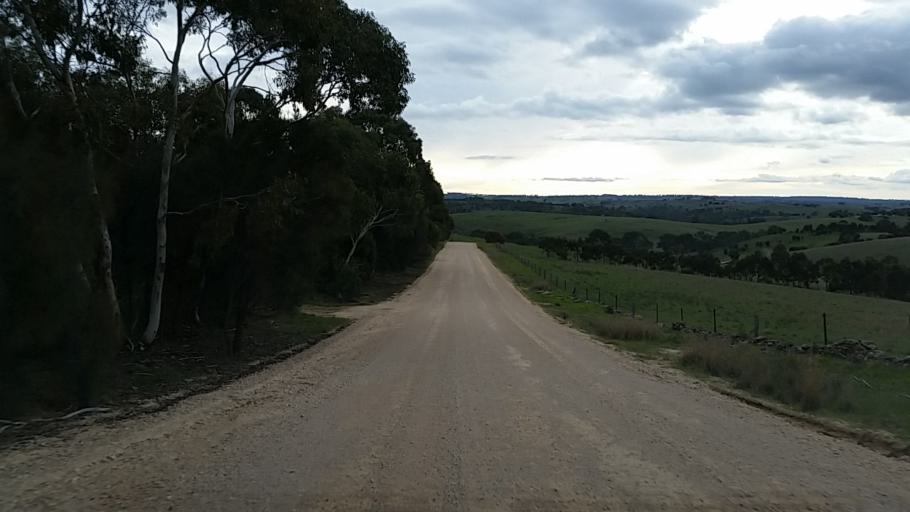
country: AU
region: South Australia
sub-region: Mount Barker
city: Callington
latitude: -34.9983
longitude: 139.0423
